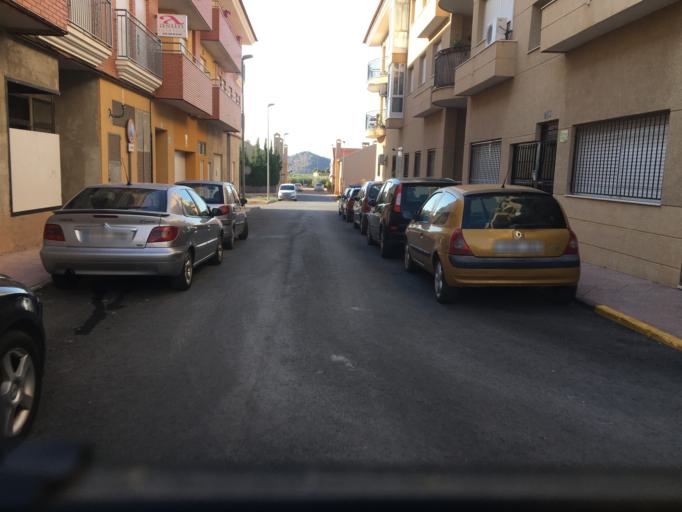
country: ES
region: Murcia
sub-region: Murcia
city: Puerto Lumbreras
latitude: 37.5642
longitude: -1.8037
